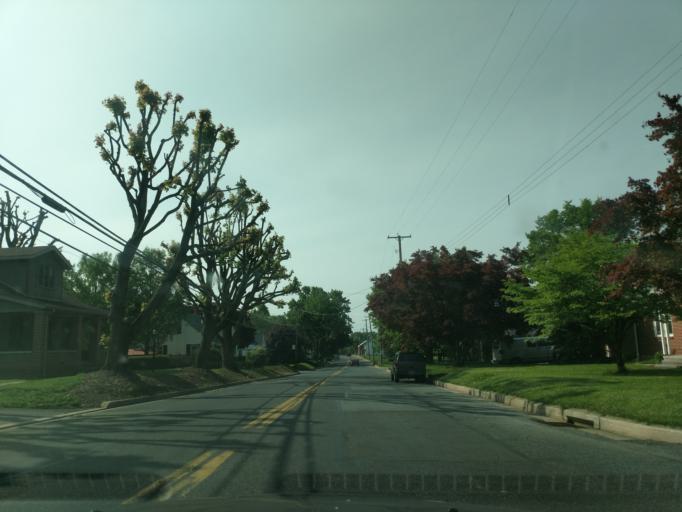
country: US
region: Pennsylvania
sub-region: Lebanon County
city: Lebanon South
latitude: 40.3285
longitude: -76.4064
